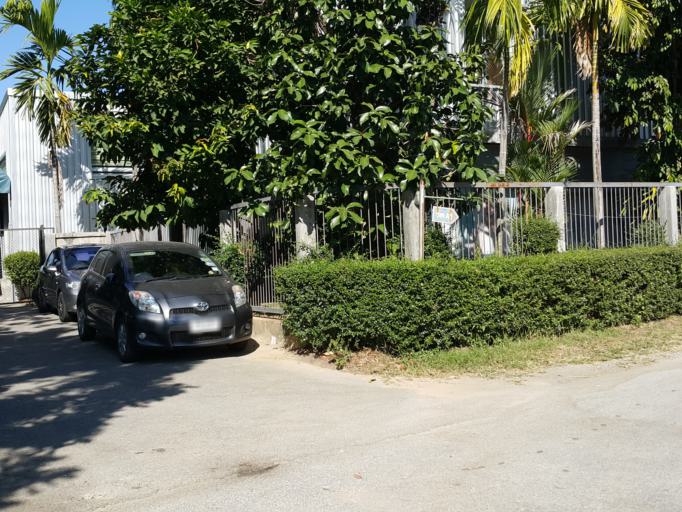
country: TH
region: Chiang Mai
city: Chiang Mai
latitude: 18.7788
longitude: 99.0306
